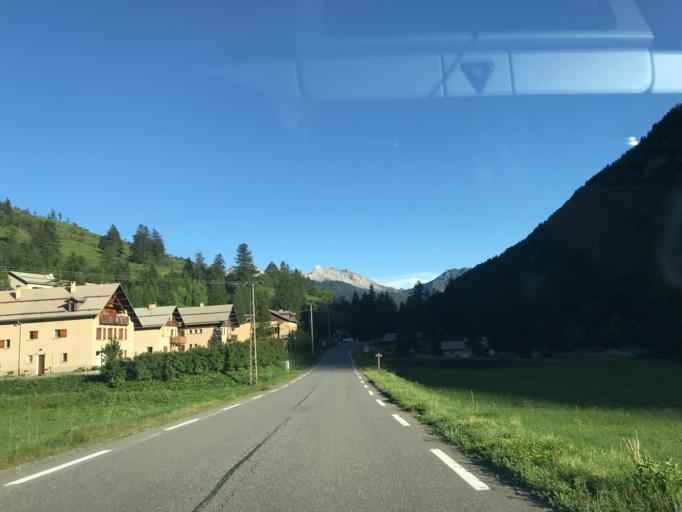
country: FR
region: Provence-Alpes-Cote d'Azur
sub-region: Departement des Hautes-Alpes
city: Guillestre
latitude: 44.7645
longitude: 6.7415
